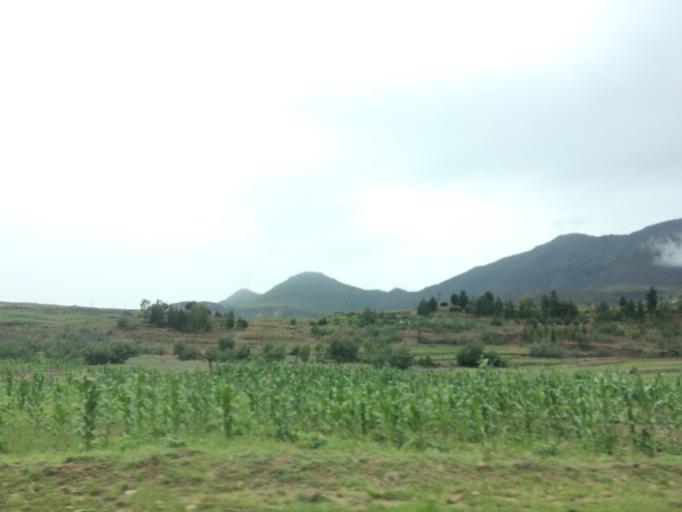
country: LS
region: Mafeteng
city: Mafeteng
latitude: -29.7816
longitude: 27.5217
